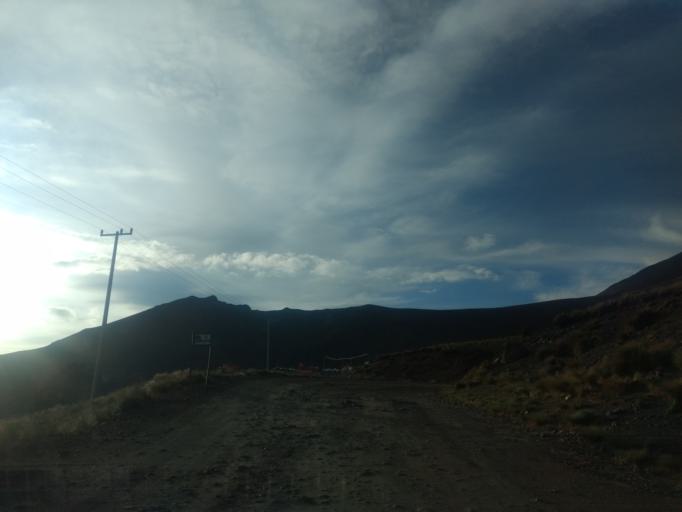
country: MX
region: Mexico
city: Cerro La Calera
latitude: 19.1200
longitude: -99.7513
